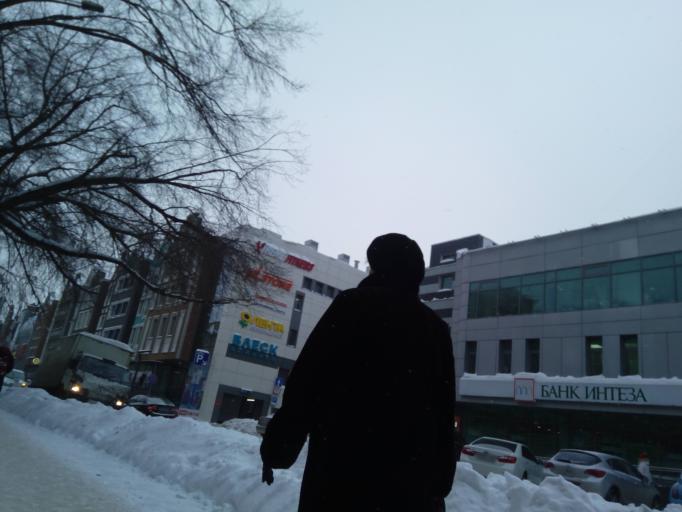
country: RU
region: Novosibirsk
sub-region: Novosibirskiy Rayon
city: Novosibirsk
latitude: 54.9908
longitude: 82.9025
